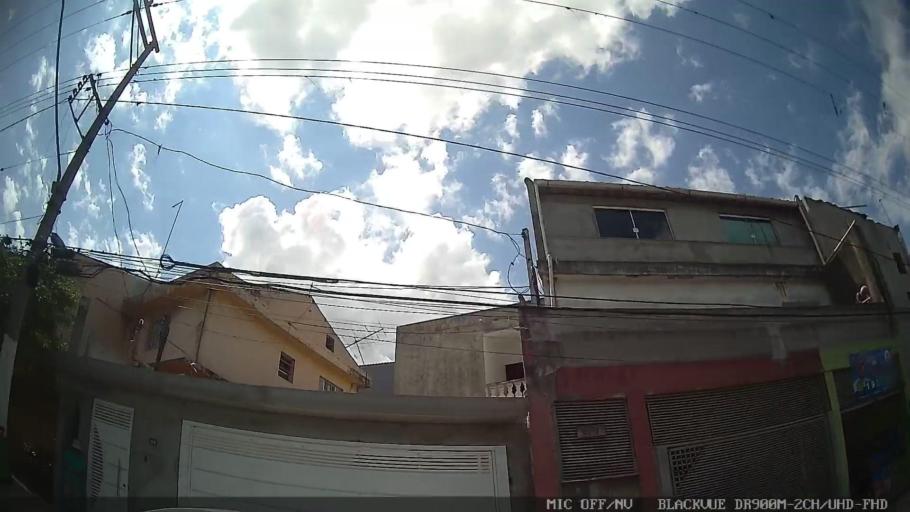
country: BR
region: Sao Paulo
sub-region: Ferraz De Vasconcelos
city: Ferraz de Vasconcelos
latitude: -23.5418
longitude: -46.4605
